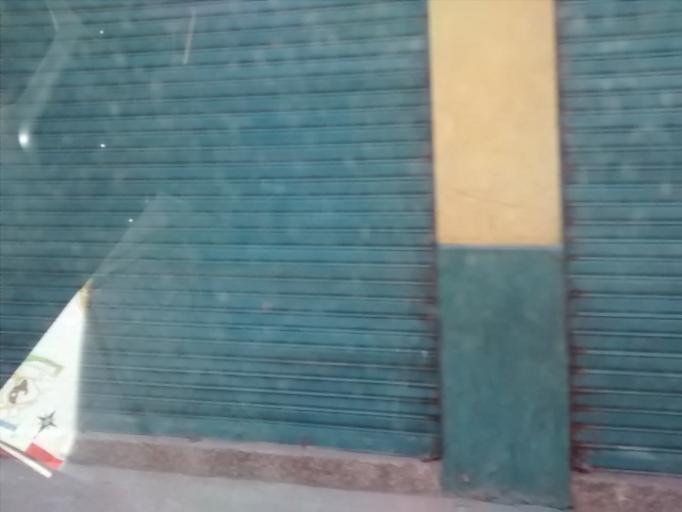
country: CO
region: Bolivar
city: Cartagena
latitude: 10.4223
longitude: -75.5456
